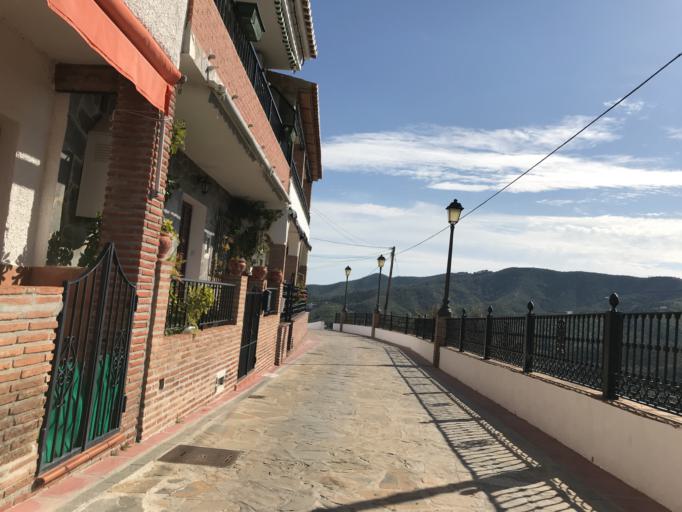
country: ES
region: Andalusia
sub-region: Provincia de Malaga
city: Valdes
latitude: 36.7699
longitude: -4.2166
